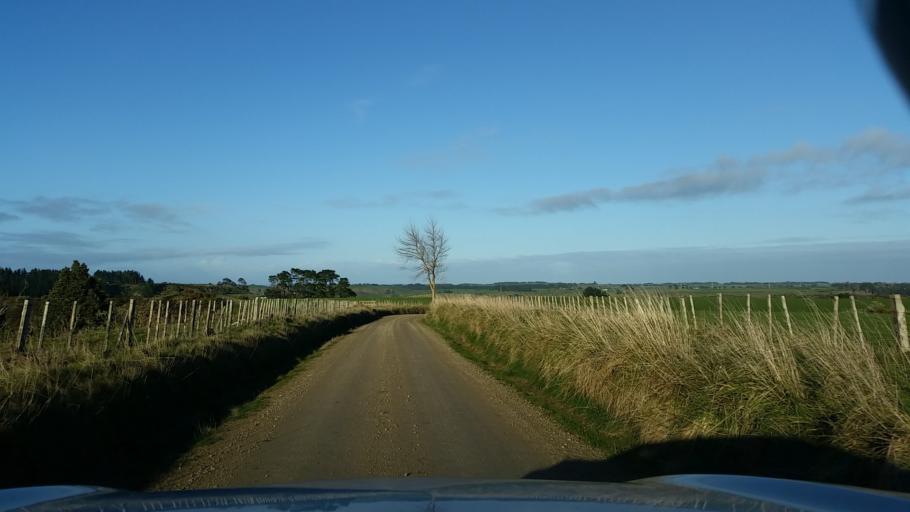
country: NZ
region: Taranaki
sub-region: South Taranaki District
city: Patea
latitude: -39.7565
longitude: 174.7432
